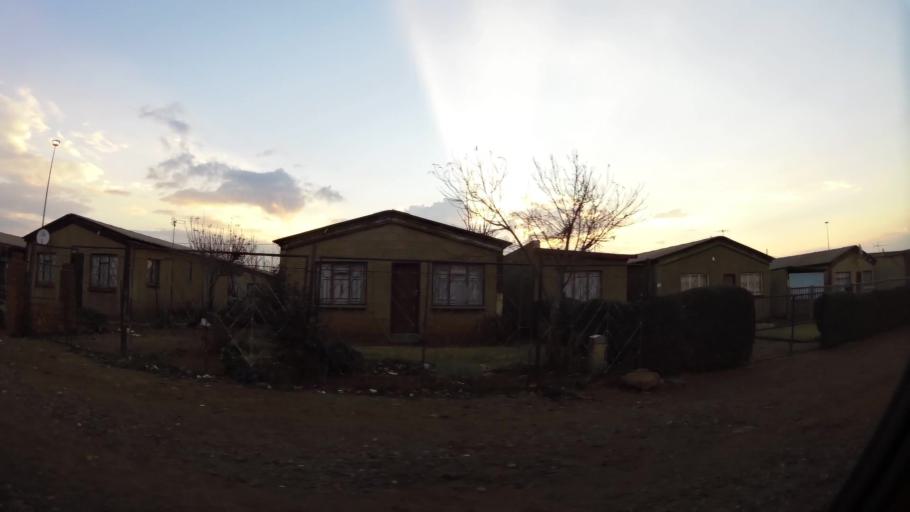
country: ZA
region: Gauteng
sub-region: City of Johannesburg Metropolitan Municipality
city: Orange Farm
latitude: -26.5530
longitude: 27.8635
